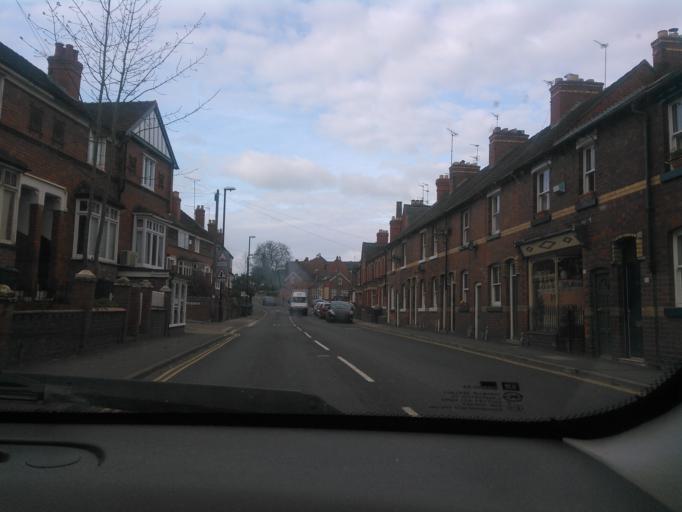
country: GB
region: England
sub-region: Shropshire
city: Shrewsbury
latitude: 52.7034
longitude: -2.7504
